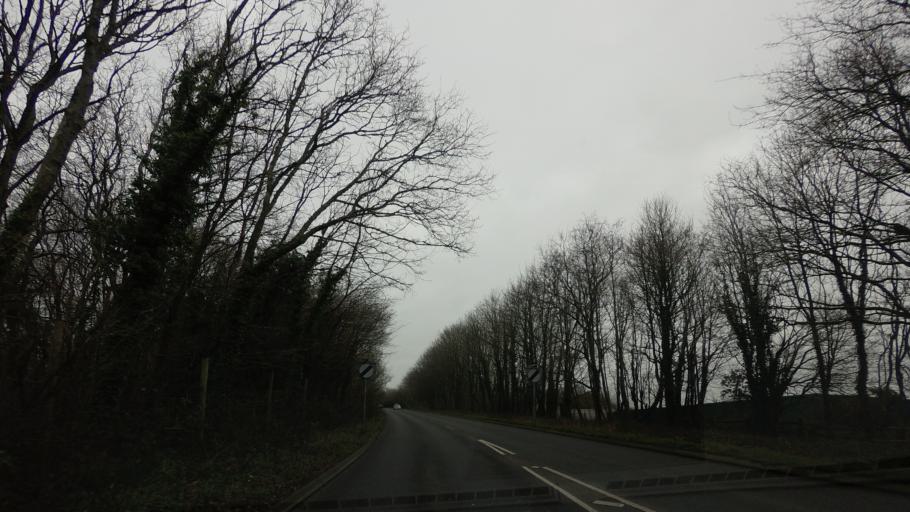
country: GB
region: England
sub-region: East Sussex
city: Saint Leonards-on-Sea
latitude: 50.8834
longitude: 0.5387
